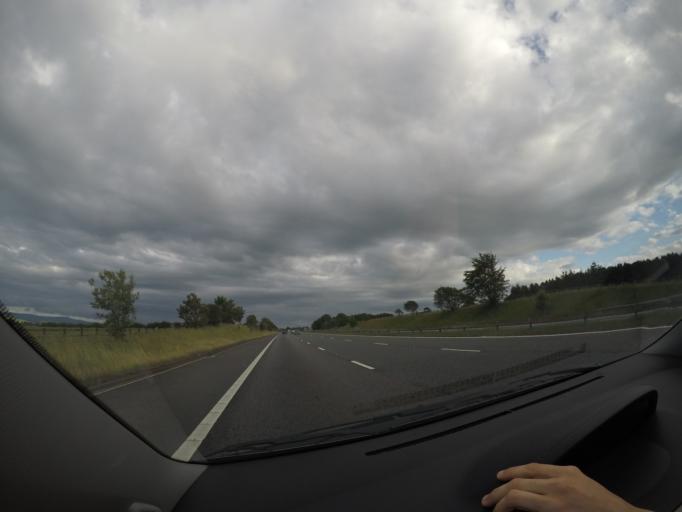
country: GB
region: England
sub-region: Cumbria
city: Scotby
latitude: 54.7846
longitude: -2.8586
